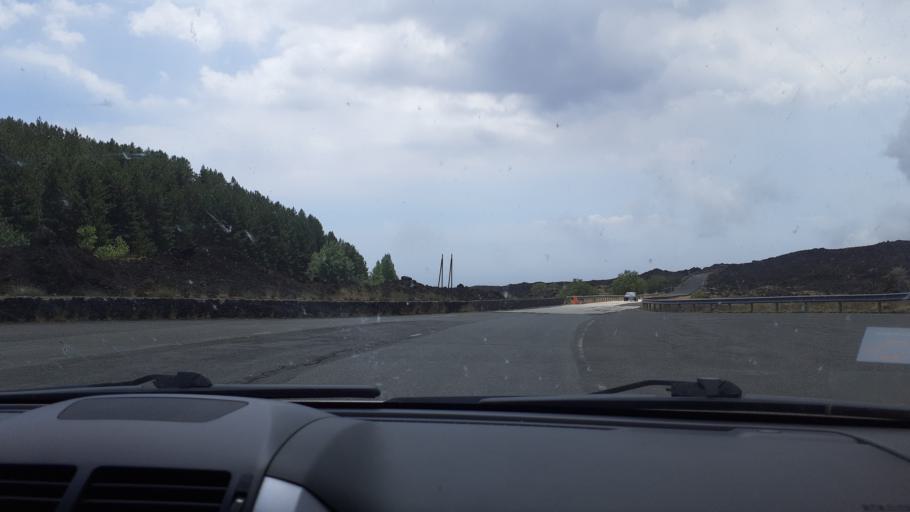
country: IT
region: Sicily
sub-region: Catania
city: Nicolosi
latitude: 37.6930
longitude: 15.0213
